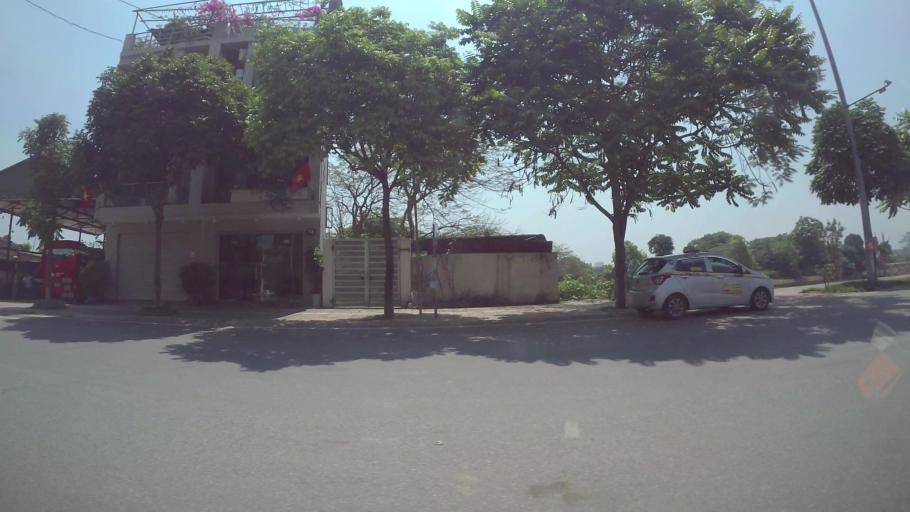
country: VN
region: Ha Noi
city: Hoan Kiem
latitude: 21.0377
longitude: 105.8822
